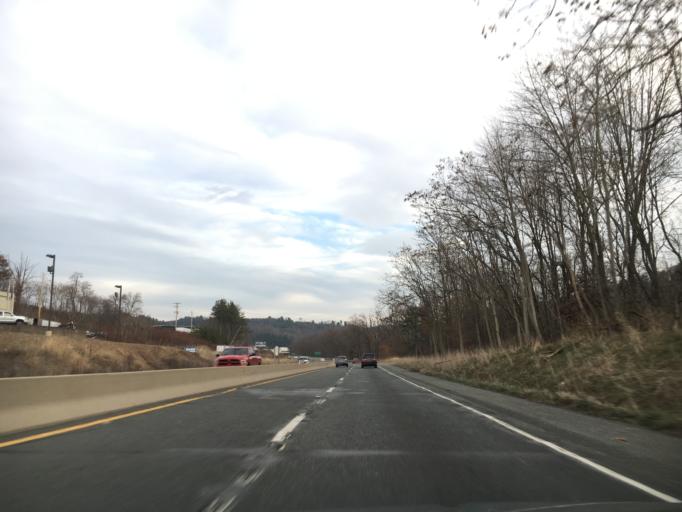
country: US
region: Pennsylvania
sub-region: Carbon County
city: Weissport East
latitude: 40.8208
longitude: -75.6856
